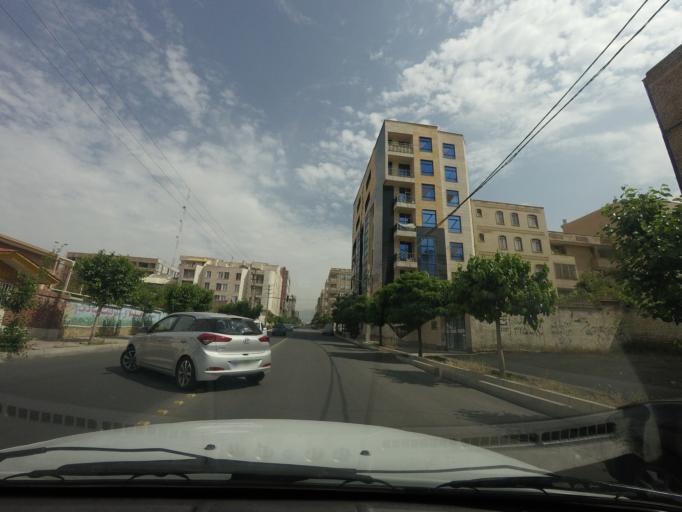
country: IR
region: Alborz
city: Karaj
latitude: 35.8383
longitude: 50.9952
